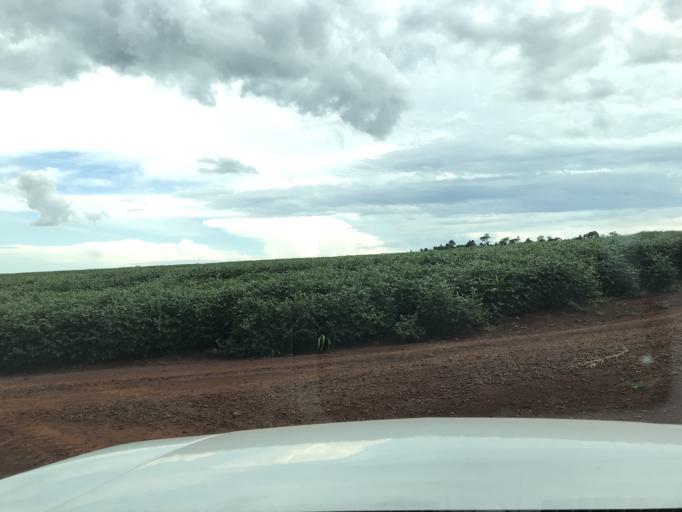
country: BR
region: Parana
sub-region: Palotina
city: Palotina
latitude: -24.2728
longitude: -53.7761
